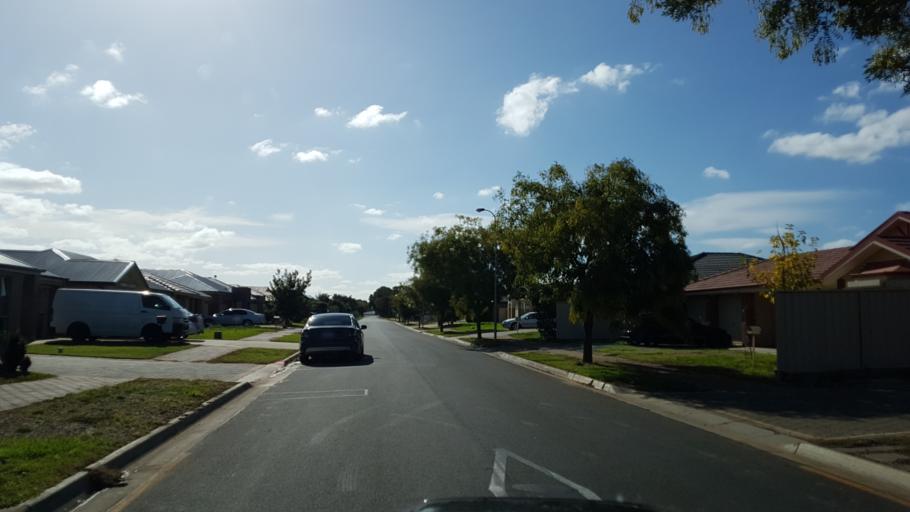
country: AU
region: South Australia
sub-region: Salisbury
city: Salisbury
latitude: -34.7665
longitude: 138.5992
